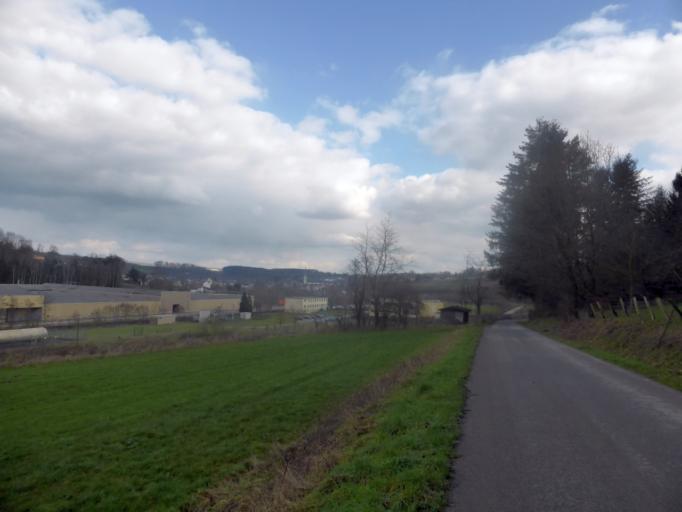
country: LU
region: Luxembourg
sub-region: Canton de Mersch
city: Bissen
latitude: 49.7830
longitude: 6.0531
